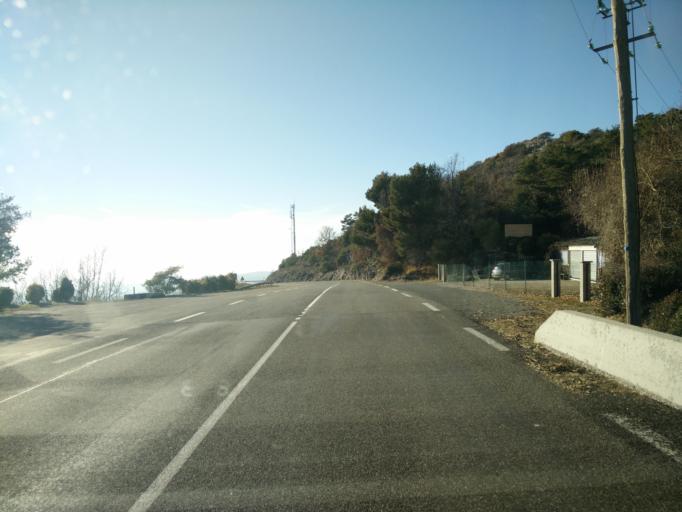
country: FR
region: Provence-Alpes-Cote d'Azur
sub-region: Departement des Alpes-Maritimes
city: Saint-Vallier-de-Thiey
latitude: 43.7112
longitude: 6.8371
